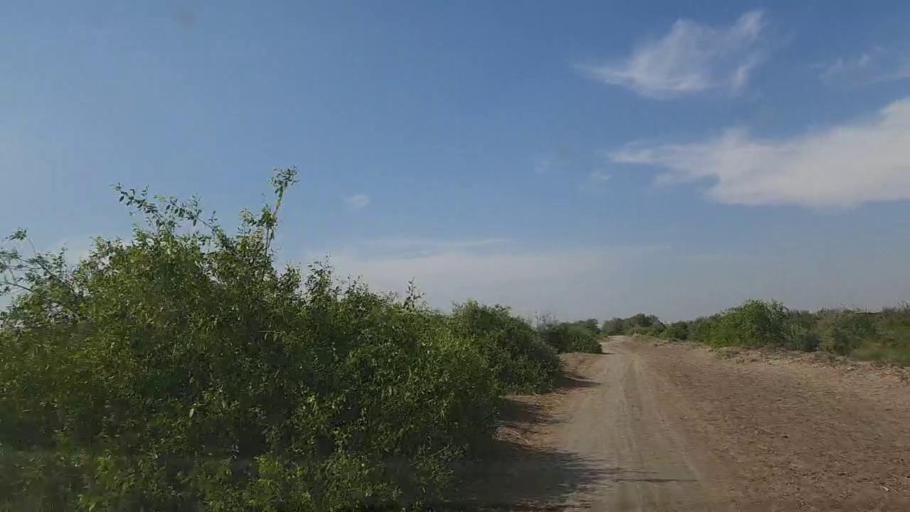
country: PK
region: Sindh
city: Mirpur Batoro
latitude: 24.8017
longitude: 68.2687
